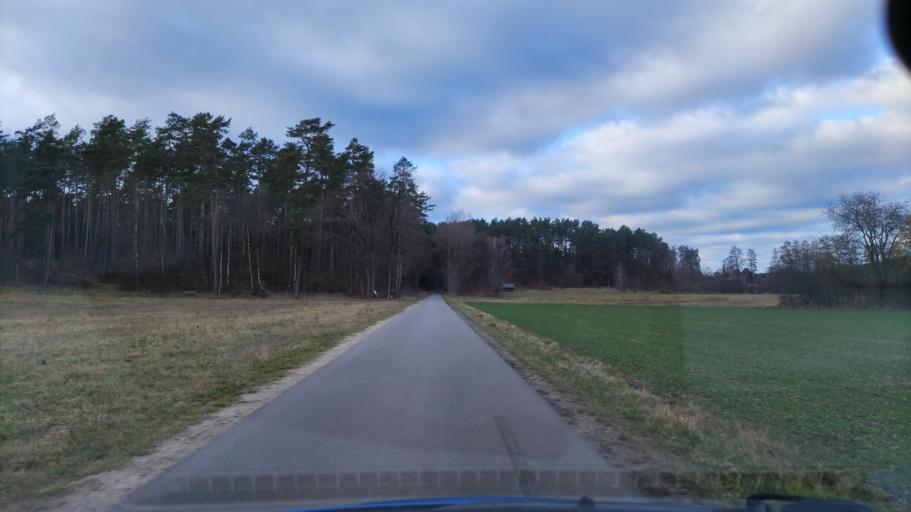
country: DE
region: Lower Saxony
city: Gohrde
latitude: 53.1500
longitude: 10.8826
